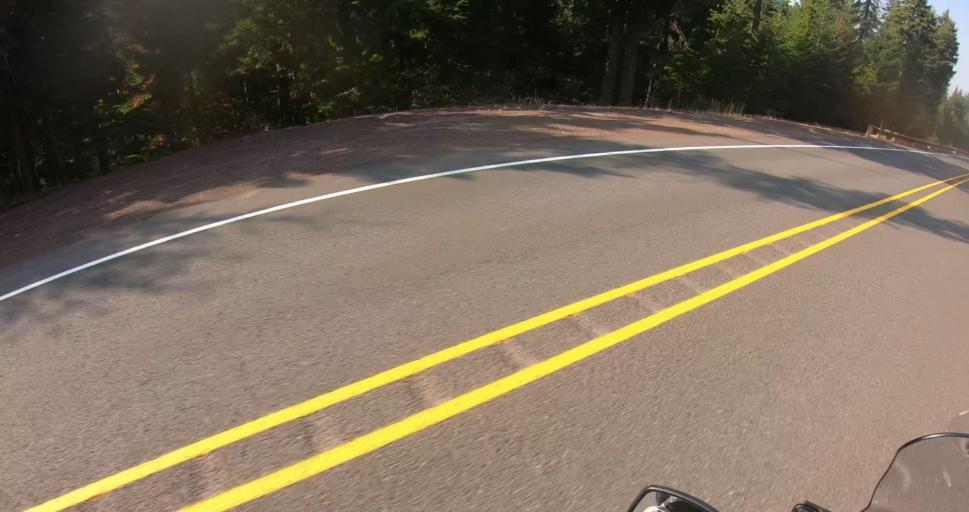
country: US
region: Oregon
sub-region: Hood River County
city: Odell
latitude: 45.3476
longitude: -121.5684
